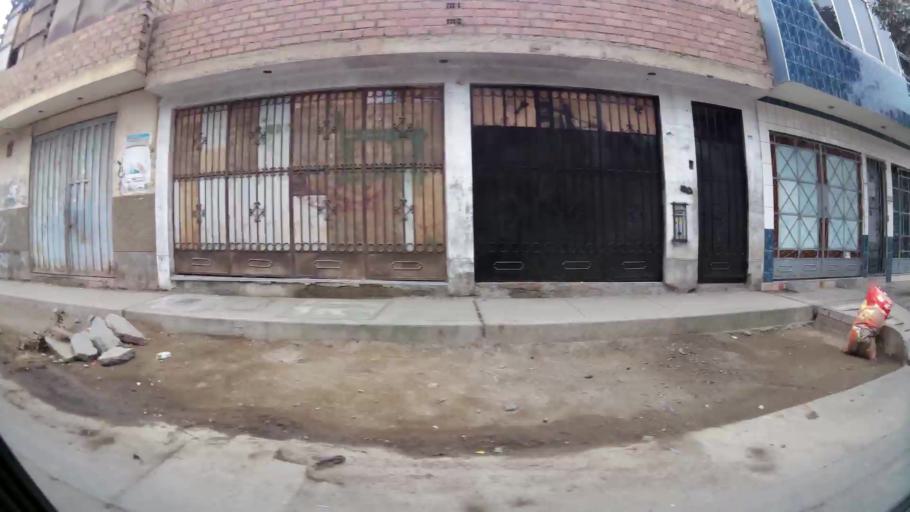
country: PE
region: Lima
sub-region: Lima
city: Independencia
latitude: -11.9528
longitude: -77.0831
